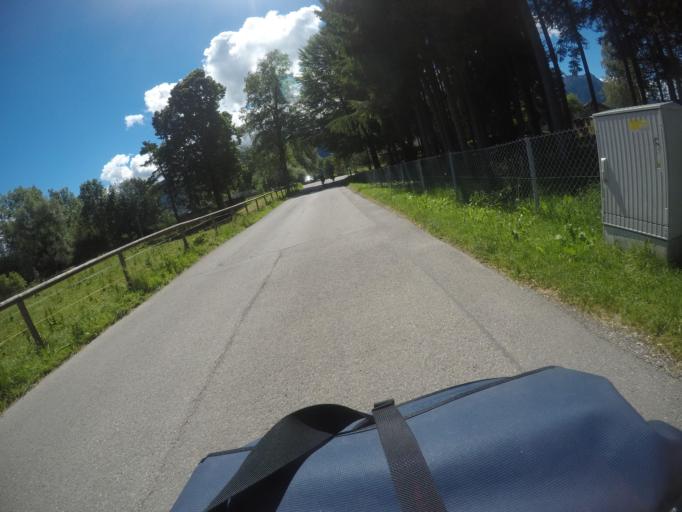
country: DE
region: Bavaria
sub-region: Swabia
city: Schwangau
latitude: 47.5921
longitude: 10.7420
